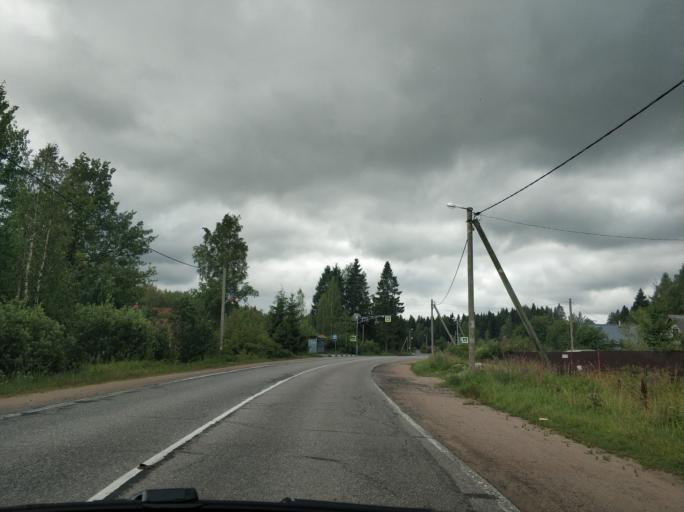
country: RU
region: Leningrad
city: Borisova Griva
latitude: 60.0913
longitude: 30.9579
